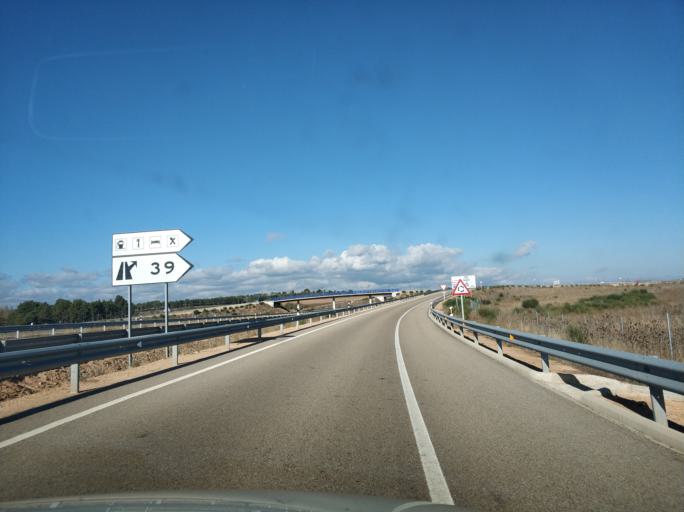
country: ES
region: Castille and Leon
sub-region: Provincia de Soria
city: Almazan
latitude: 41.4685
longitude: -2.5241
